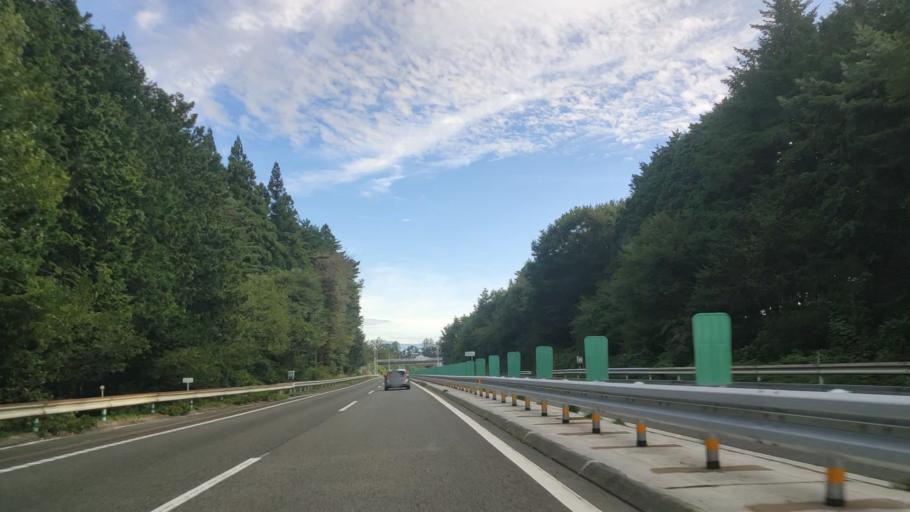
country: JP
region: Nagano
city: Ina
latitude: 35.7124
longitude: 137.9075
